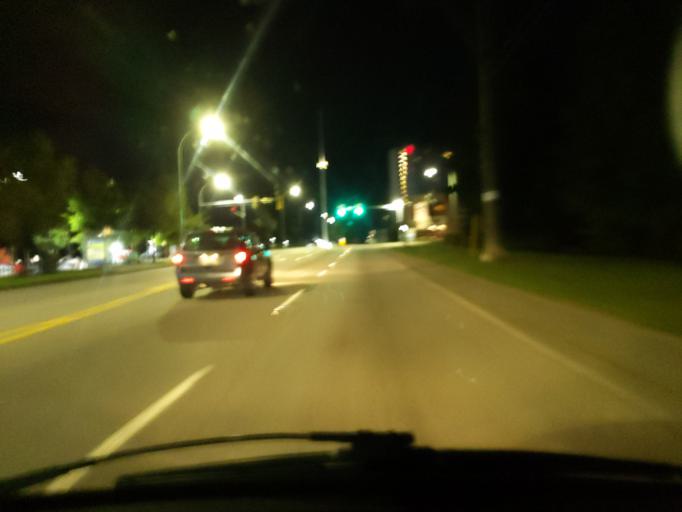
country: CA
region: British Columbia
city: Surrey
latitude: 49.1916
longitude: -122.7942
